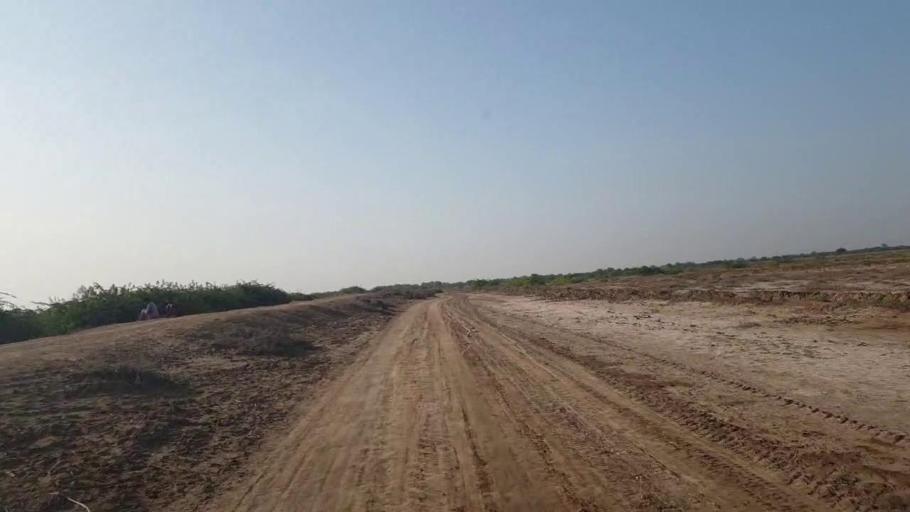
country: PK
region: Sindh
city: Badin
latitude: 24.4644
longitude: 68.7378
